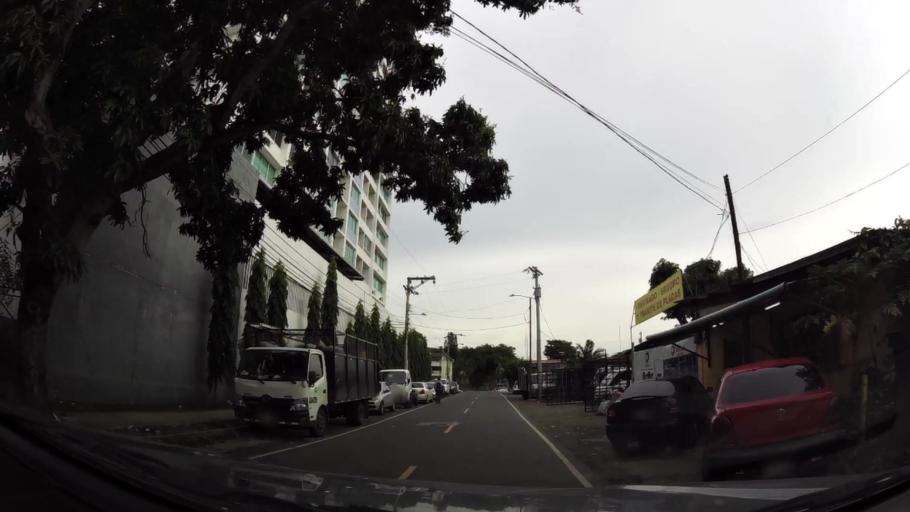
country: PA
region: Panama
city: Panama
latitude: 9.0058
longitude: -79.4970
